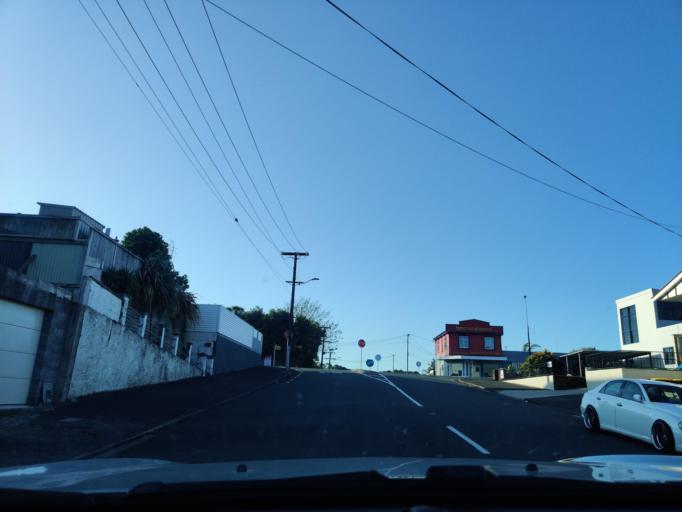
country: NZ
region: Taranaki
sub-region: New Plymouth District
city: New Plymouth
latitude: -39.0591
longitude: 174.0621
